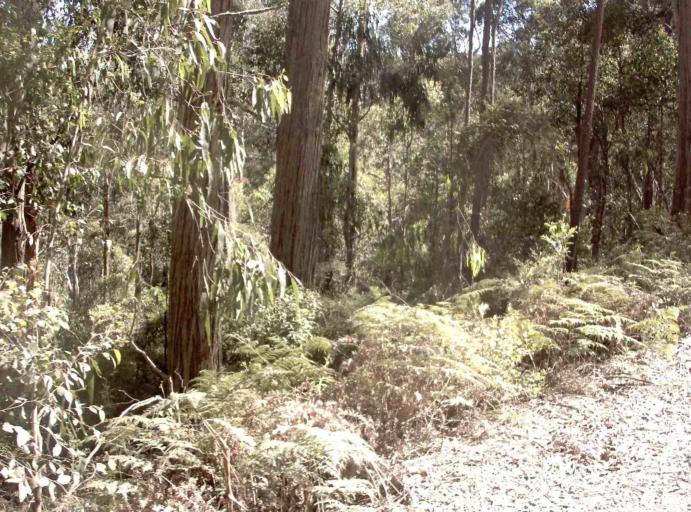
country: AU
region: New South Wales
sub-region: Bombala
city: Bombala
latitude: -37.2508
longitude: 148.7409
